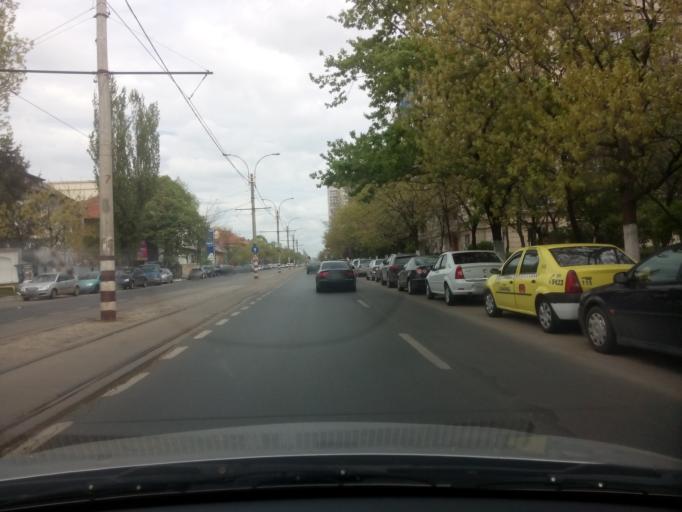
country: RO
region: Bucuresti
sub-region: Municipiul Bucuresti
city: Bucharest
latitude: 44.4551
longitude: 26.1052
